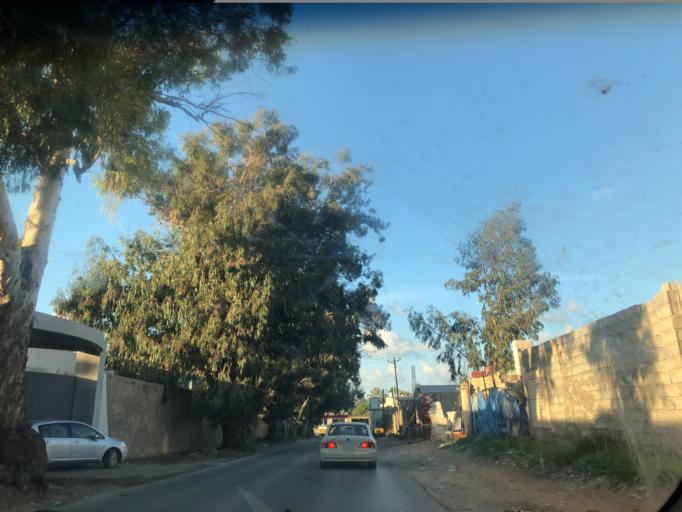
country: LY
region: Tripoli
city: Tagiura
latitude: 32.8646
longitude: 13.2782
